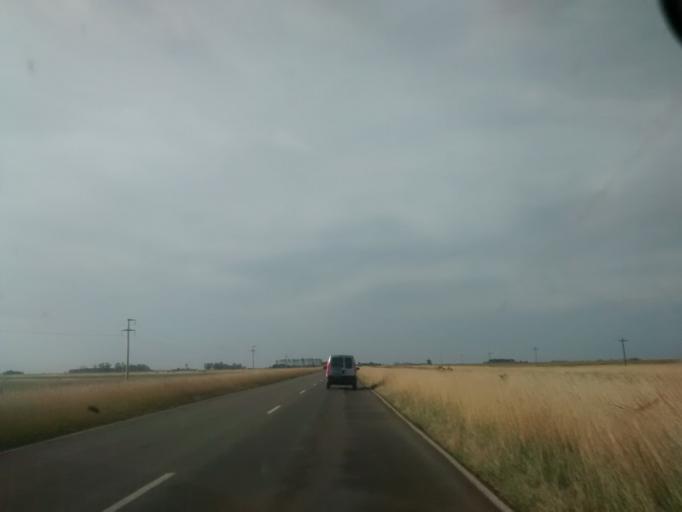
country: AR
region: Buenos Aires
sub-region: Partido de Ayacucho
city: Ayacucho
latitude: -36.9098
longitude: -58.5262
